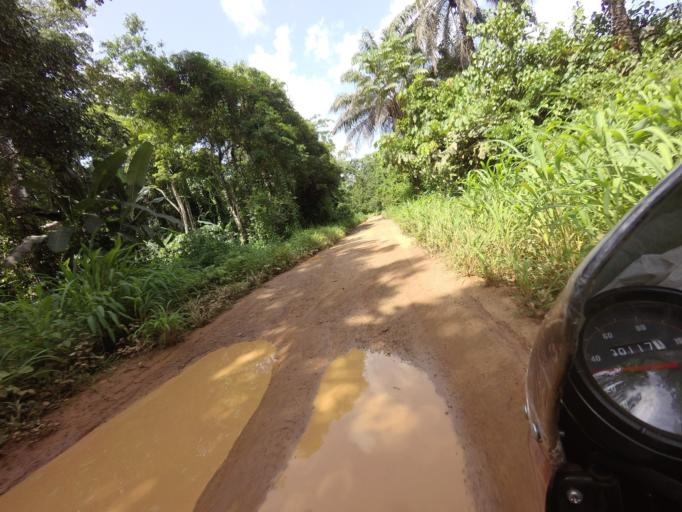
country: SL
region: Eastern Province
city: Manowa
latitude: 8.1480
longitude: -10.7735
